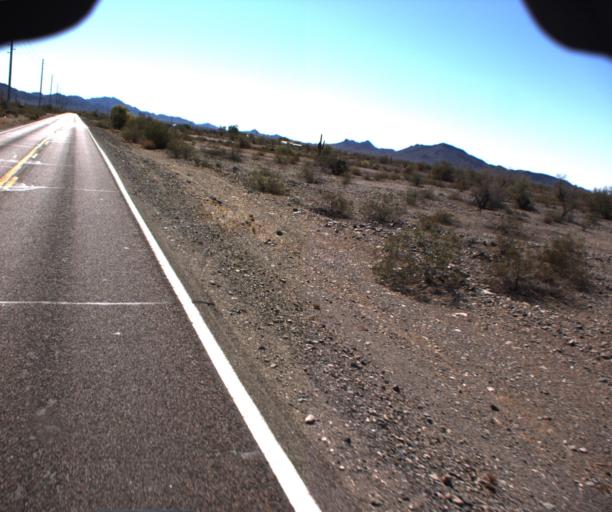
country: US
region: Arizona
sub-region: La Paz County
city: Salome
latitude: 33.7463
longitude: -113.7596
